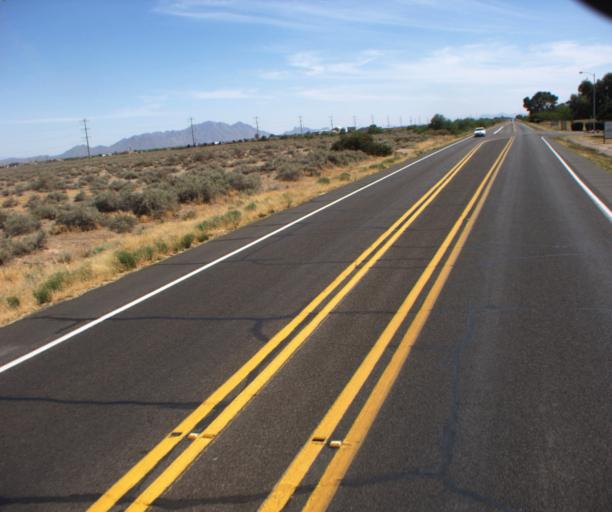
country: US
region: Arizona
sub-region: Pinal County
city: Coolidge
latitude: 32.9058
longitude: -111.5151
